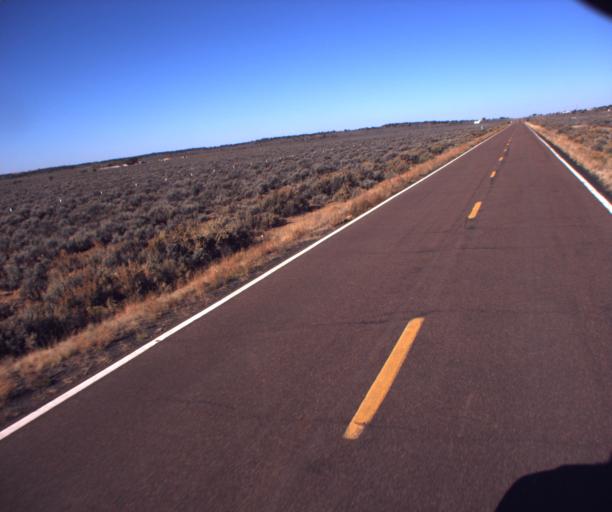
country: US
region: Arizona
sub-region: Apache County
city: Ganado
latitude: 35.7517
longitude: -109.9424
